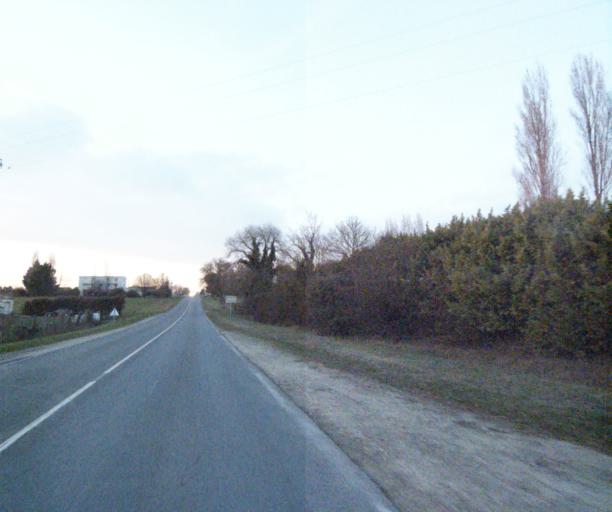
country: FR
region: Poitou-Charentes
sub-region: Departement de la Charente-Maritime
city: Saint-Porchaire
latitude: 45.8159
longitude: -0.7741
